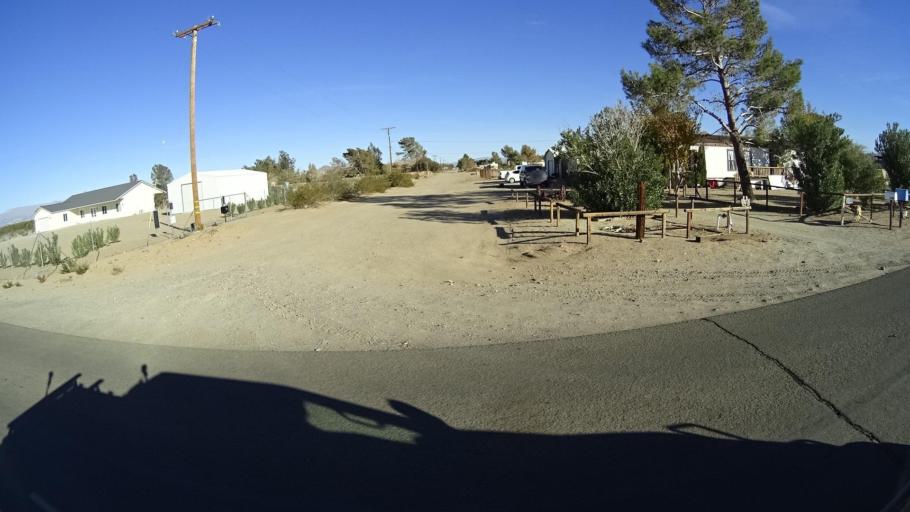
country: US
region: California
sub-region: Kern County
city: Ridgecrest
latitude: 35.6461
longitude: -117.7058
